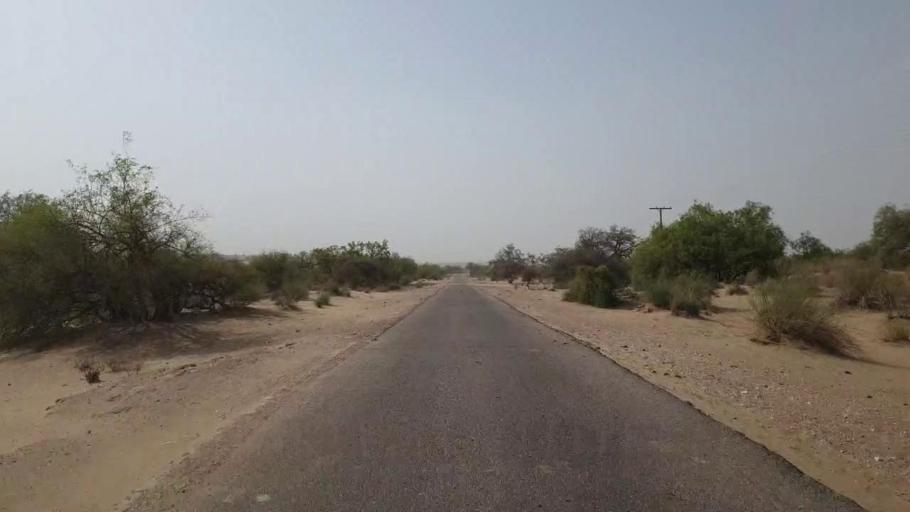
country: PK
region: Sindh
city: Mithi
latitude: 24.6014
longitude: 69.9234
